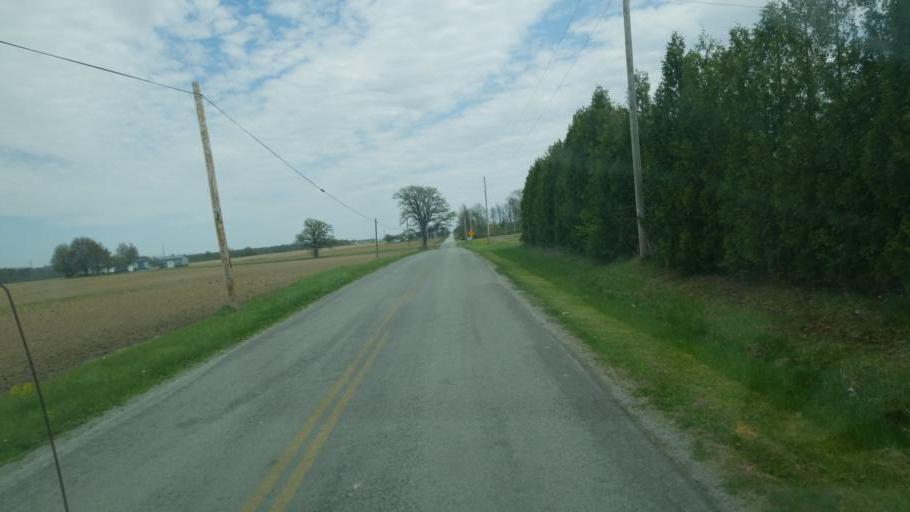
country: US
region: Ohio
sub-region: Hardin County
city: Ada
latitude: 40.8198
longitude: -83.8275
